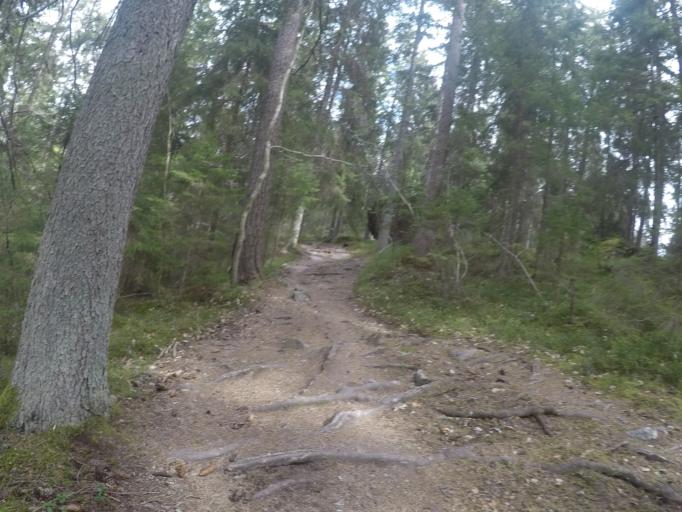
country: SE
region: Vaestmanland
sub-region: Vasteras
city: Vasteras
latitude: 59.6295
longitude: 16.5184
